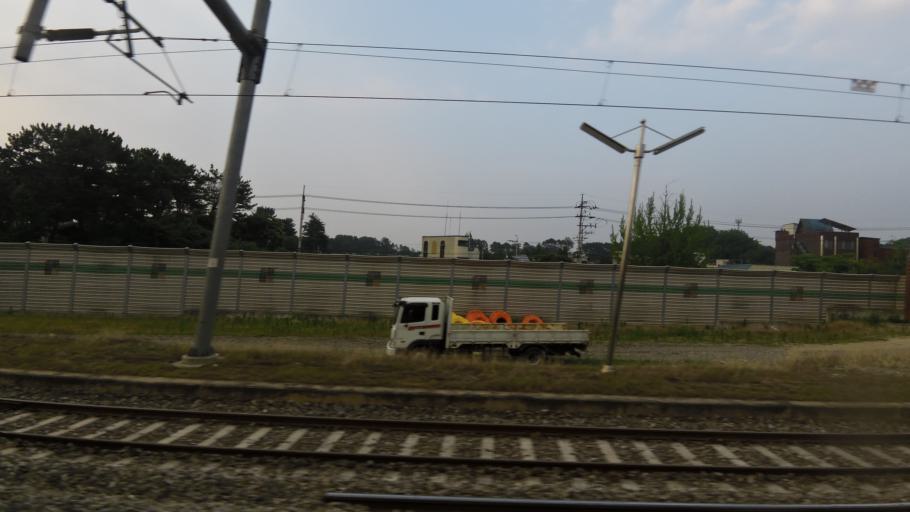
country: KR
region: Daejeon
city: Songgang-dong
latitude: 36.5581
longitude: 127.3242
